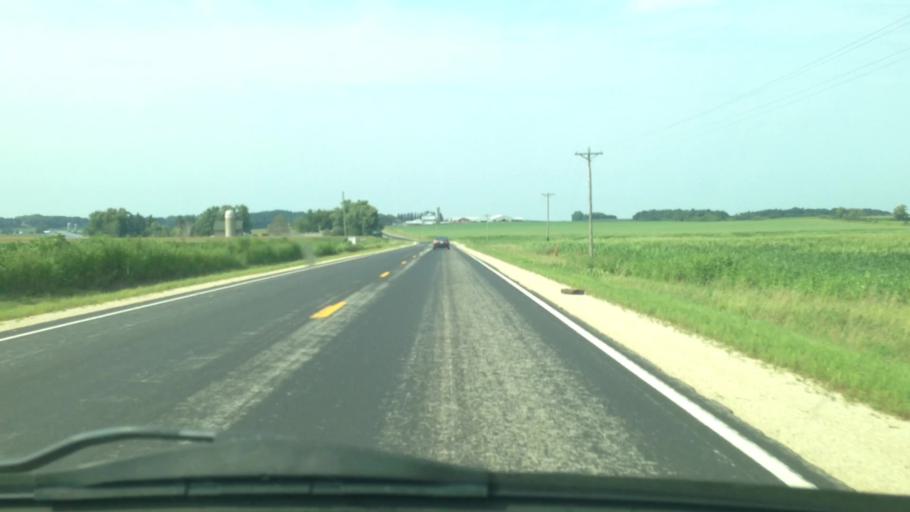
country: US
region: Minnesota
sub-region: Winona County
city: Lewiston
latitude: 43.9465
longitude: -91.9547
